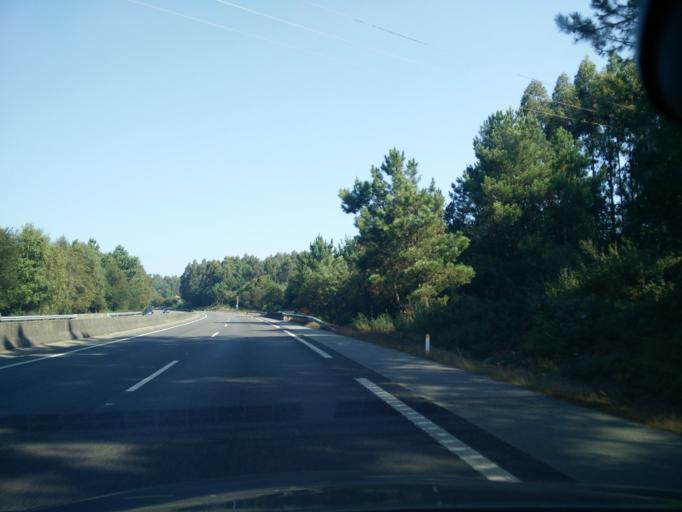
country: ES
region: Galicia
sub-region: Provincia da Coruna
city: Mino
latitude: 43.3811
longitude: -8.1798
